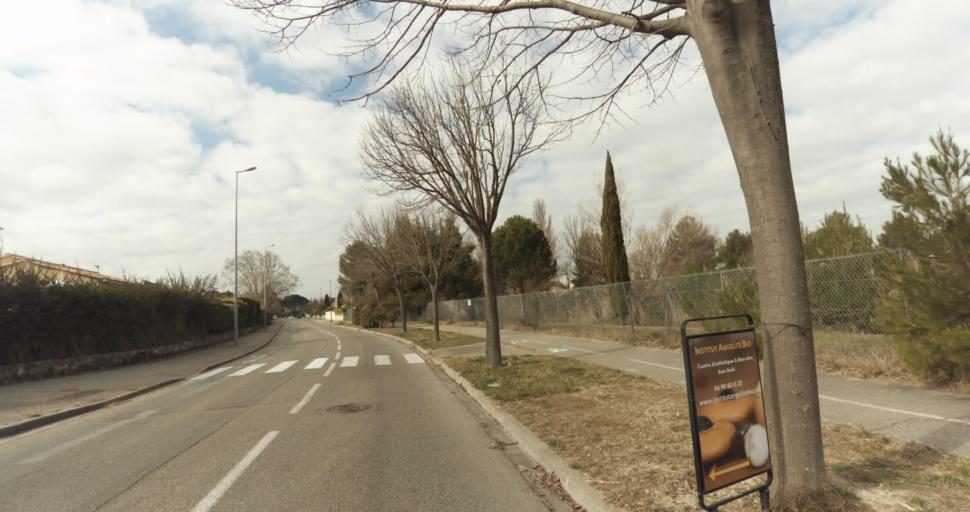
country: FR
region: Provence-Alpes-Cote d'Azur
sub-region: Departement du Vaucluse
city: Le Pontet
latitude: 43.9495
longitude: 4.8488
